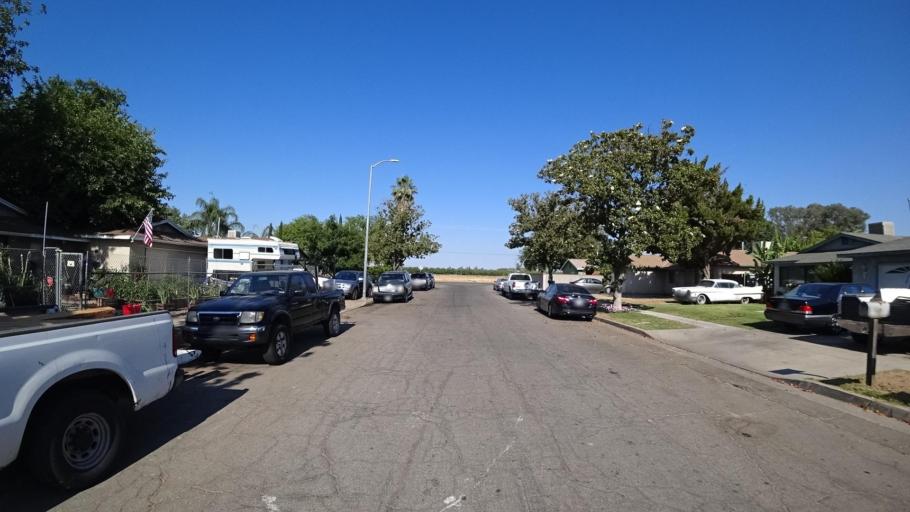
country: US
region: California
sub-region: Fresno County
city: West Park
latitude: 36.7273
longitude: -119.8303
